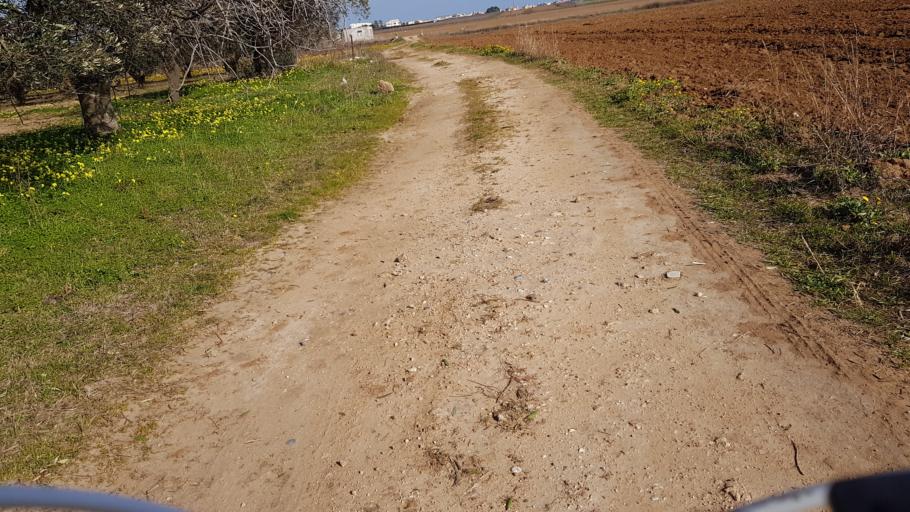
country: IT
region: Apulia
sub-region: Provincia di Brindisi
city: Brindisi
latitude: 40.6062
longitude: 17.8944
